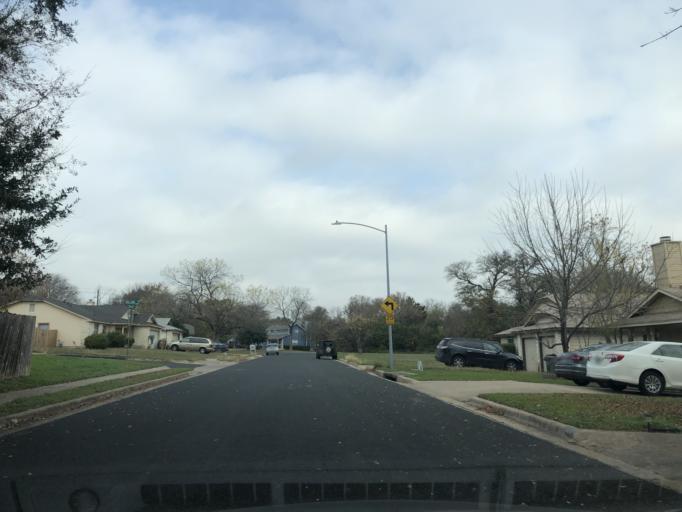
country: US
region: Texas
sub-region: Travis County
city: Wells Branch
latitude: 30.4228
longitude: -97.6849
